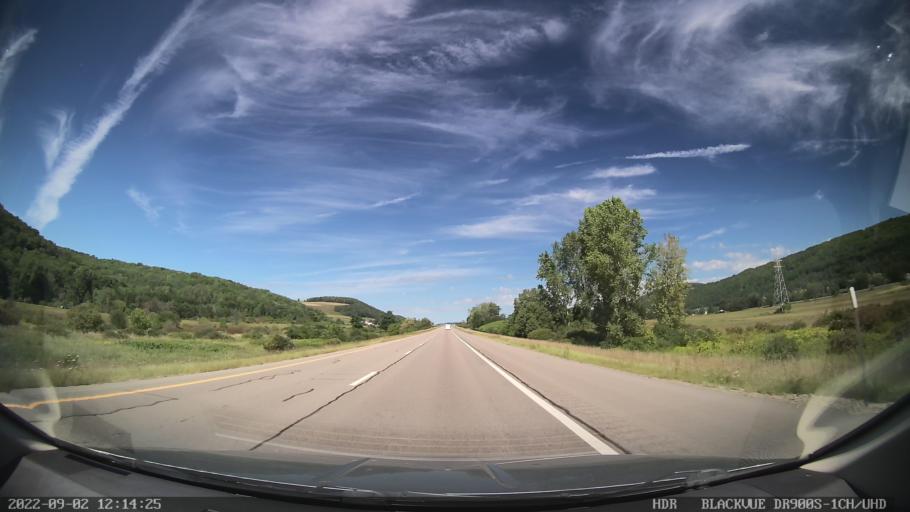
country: US
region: New York
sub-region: Steuben County
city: Wayland
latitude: 42.4519
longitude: -77.4757
